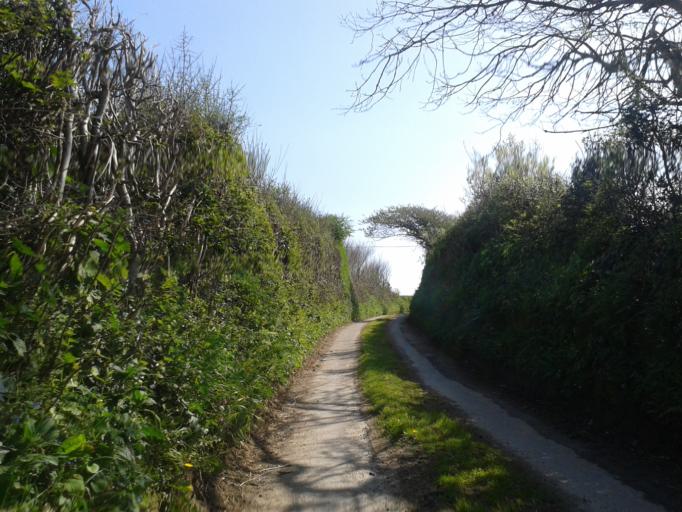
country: GB
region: England
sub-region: Devon
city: Braunton
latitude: 51.1175
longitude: -4.1752
